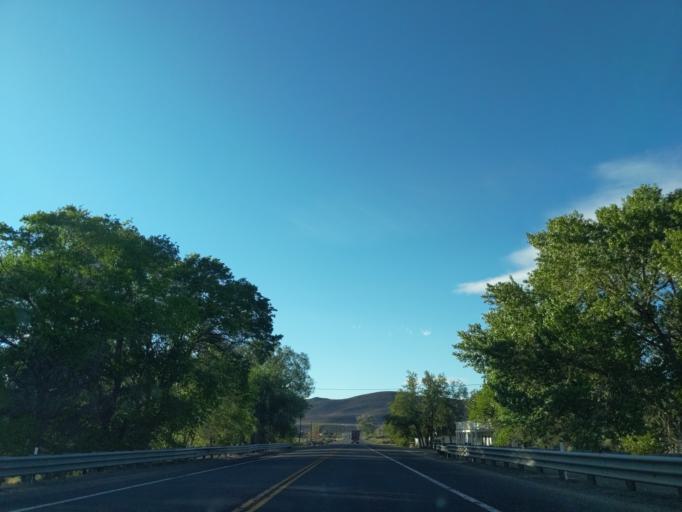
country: US
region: Nevada
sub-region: Lyon County
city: Silver Springs
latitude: 39.2936
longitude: -119.2515
